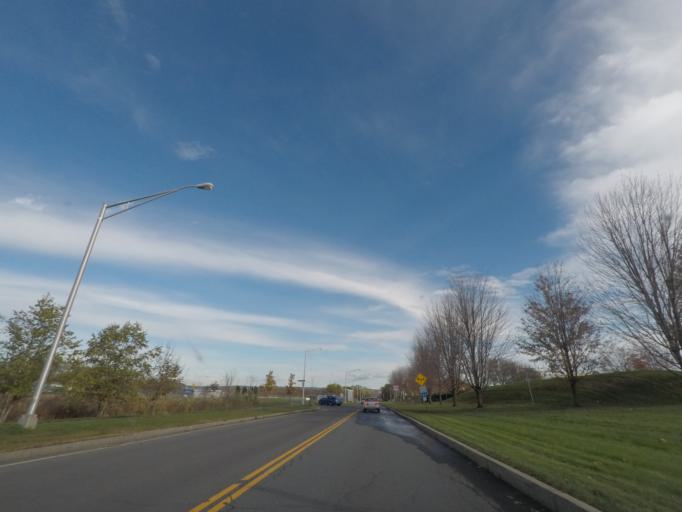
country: US
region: New York
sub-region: Albany County
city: Albany
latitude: 42.6355
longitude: -73.7752
